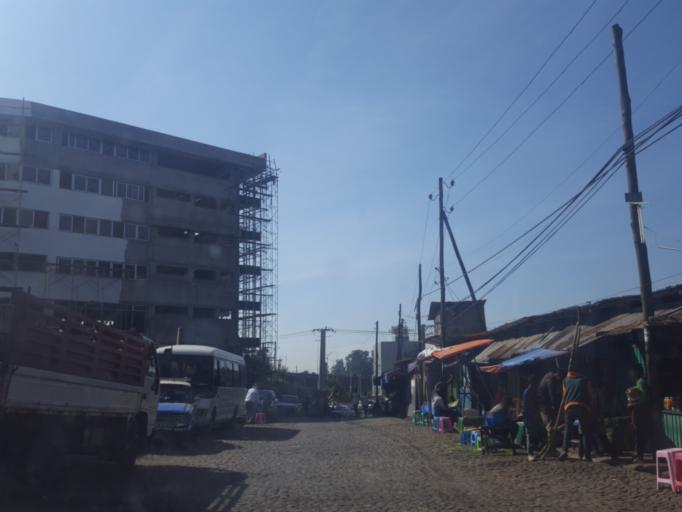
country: ET
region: Adis Abeba
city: Addis Ababa
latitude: 9.0587
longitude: 38.7131
